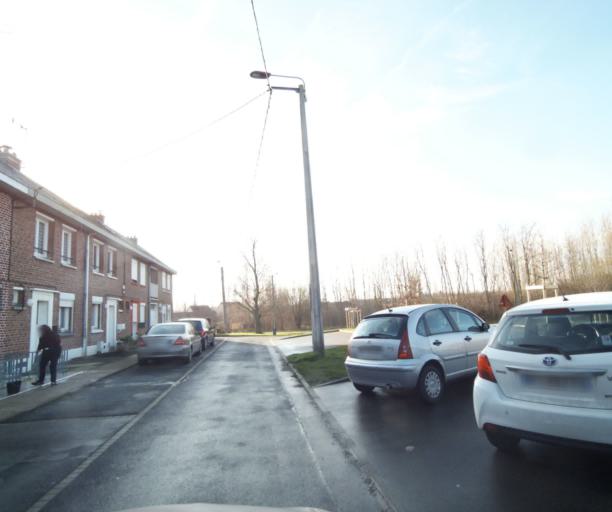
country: FR
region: Nord-Pas-de-Calais
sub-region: Departement du Nord
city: Marly
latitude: 50.3436
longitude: 3.5456
